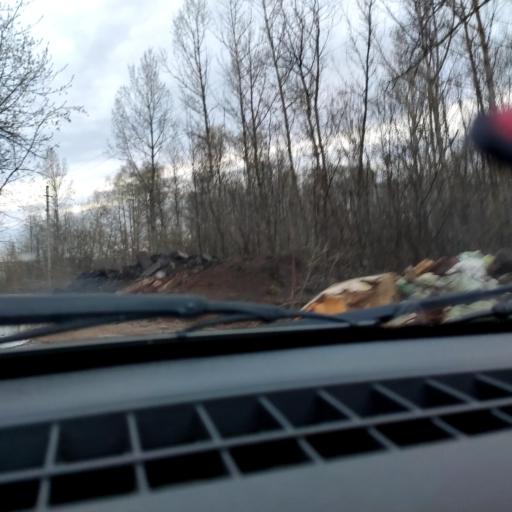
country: RU
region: Bashkortostan
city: Ufa
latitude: 54.6769
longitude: 55.9508
